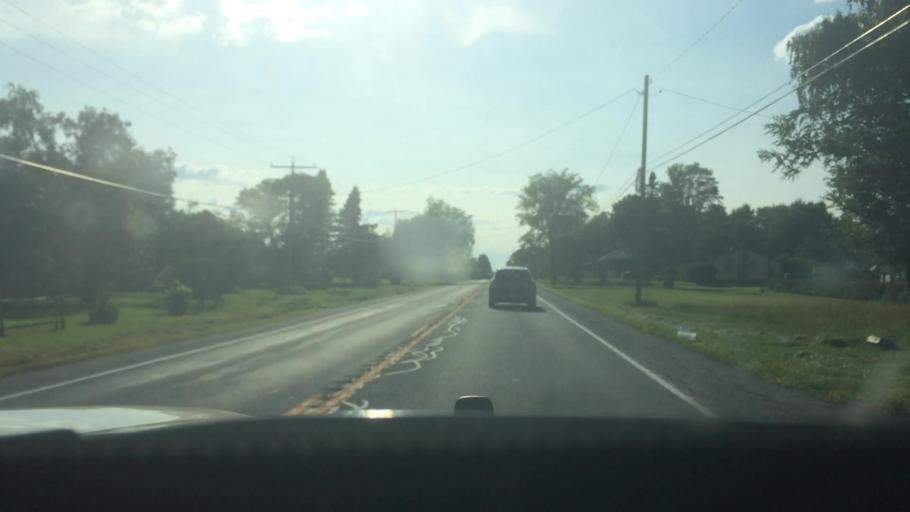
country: US
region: New York
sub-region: St. Lawrence County
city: Potsdam
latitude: 44.6702
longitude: -74.9251
